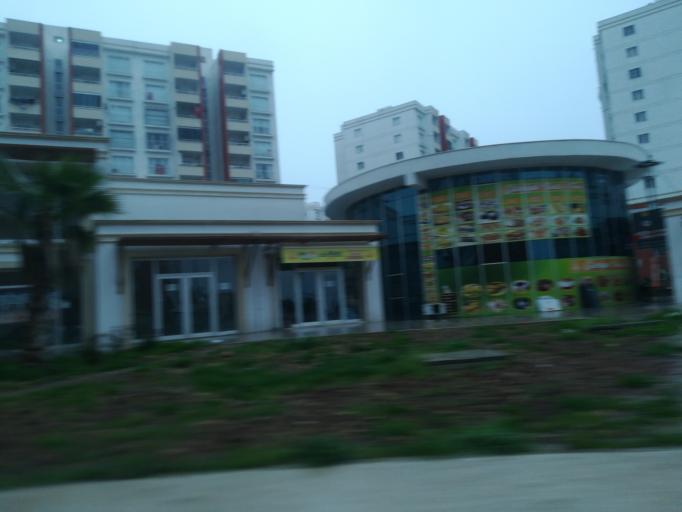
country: TR
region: Adana
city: Seyhan
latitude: 37.0088
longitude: 35.2773
